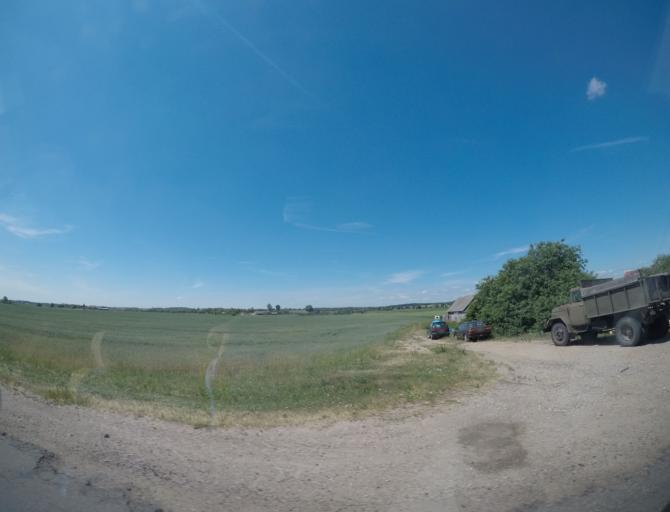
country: BY
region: Grodnenskaya
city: Hrodna
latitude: 53.7534
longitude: 23.9387
